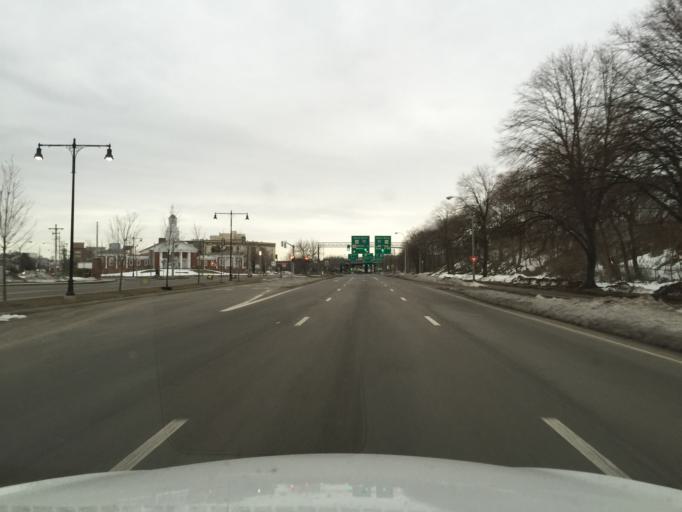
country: US
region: Massachusetts
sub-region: Middlesex County
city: Somerville
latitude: 42.3976
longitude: -71.0846
